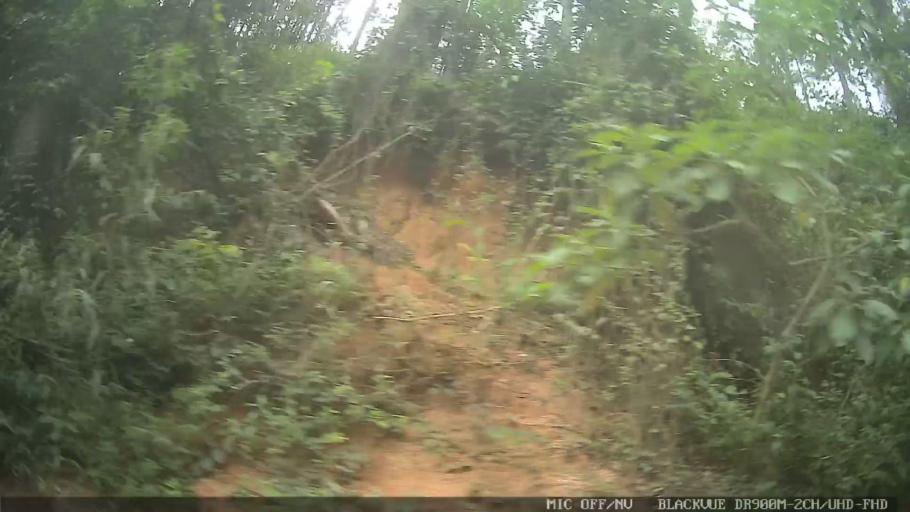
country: BR
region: Sao Paulo
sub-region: Bom Jesus Dos Perdoes
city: Bom Jesus dos Perdoes
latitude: -23.1669
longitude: -46.5118
